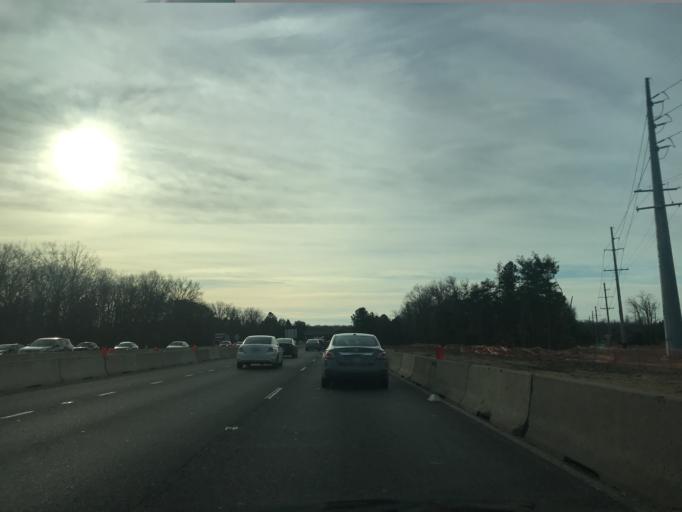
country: US
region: Maryland
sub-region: Prince George's County
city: Brandywine
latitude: 38.6991
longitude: -76.8746
